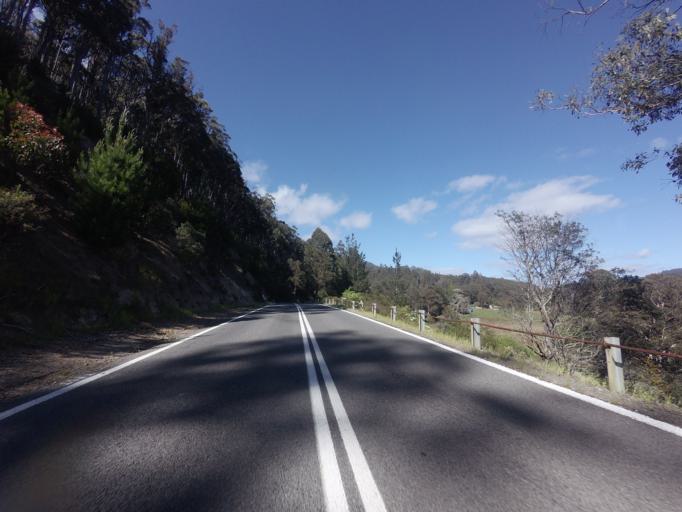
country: AU
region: Tasmania
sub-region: Derwent Valley
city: New Norfolk
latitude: -42.7102
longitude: 146.7057
